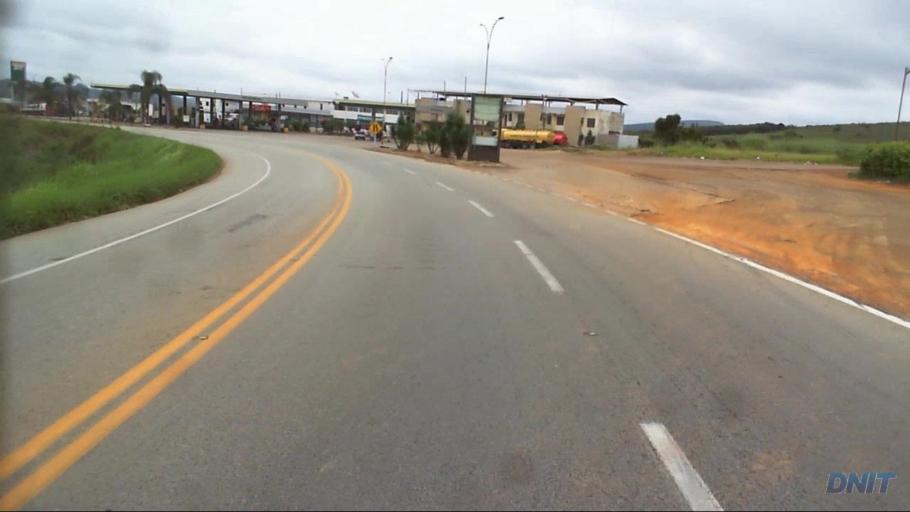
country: BR
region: Minas Gerais
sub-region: Nova Era
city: Nova Era
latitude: -19.8071
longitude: -43.0643
